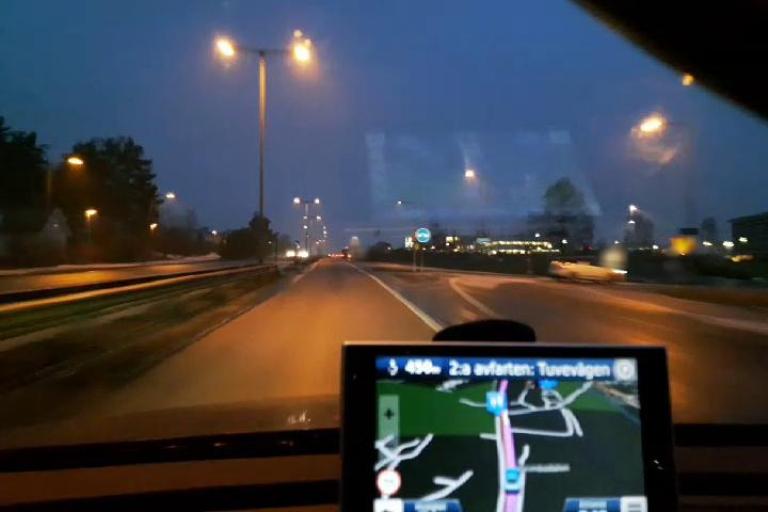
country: SE
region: Vaestra Goetaland
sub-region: Goteborg
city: Goeteborg
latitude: 57.7414
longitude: 11.9412
